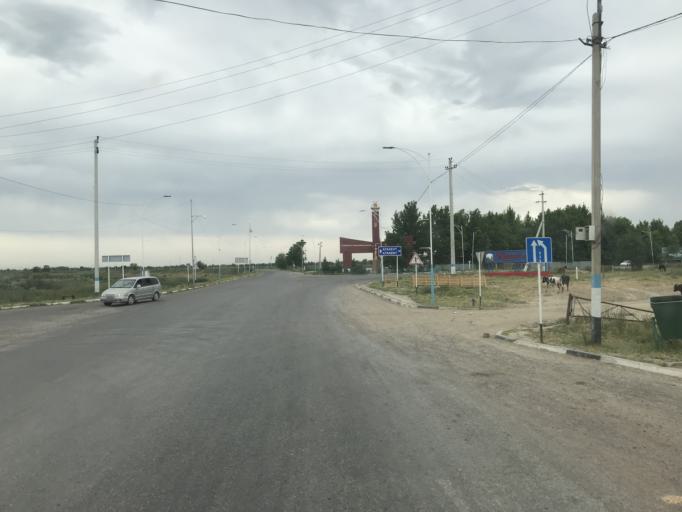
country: KZ
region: Ongtustik Qazaqstan
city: Asykata
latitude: 40.9573
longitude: 68.4637
